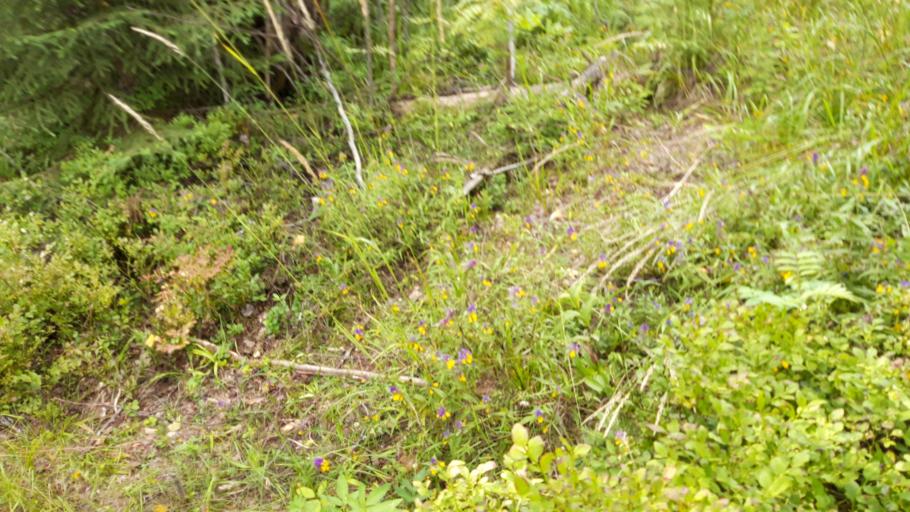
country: RU
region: Tverskaya
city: Konakovo
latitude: 56.6864
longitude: 36.7108
